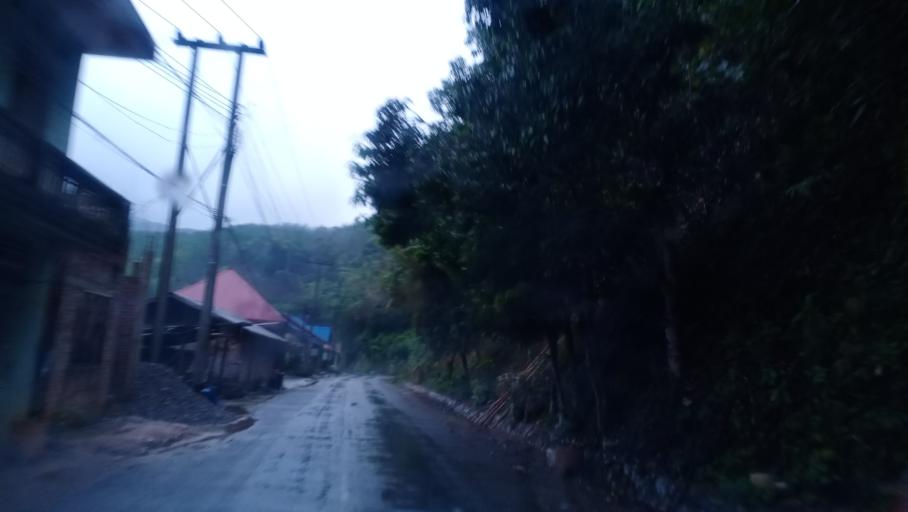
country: LA
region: Phongsali
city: Khoa
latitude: 21.0794
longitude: 102.5010
